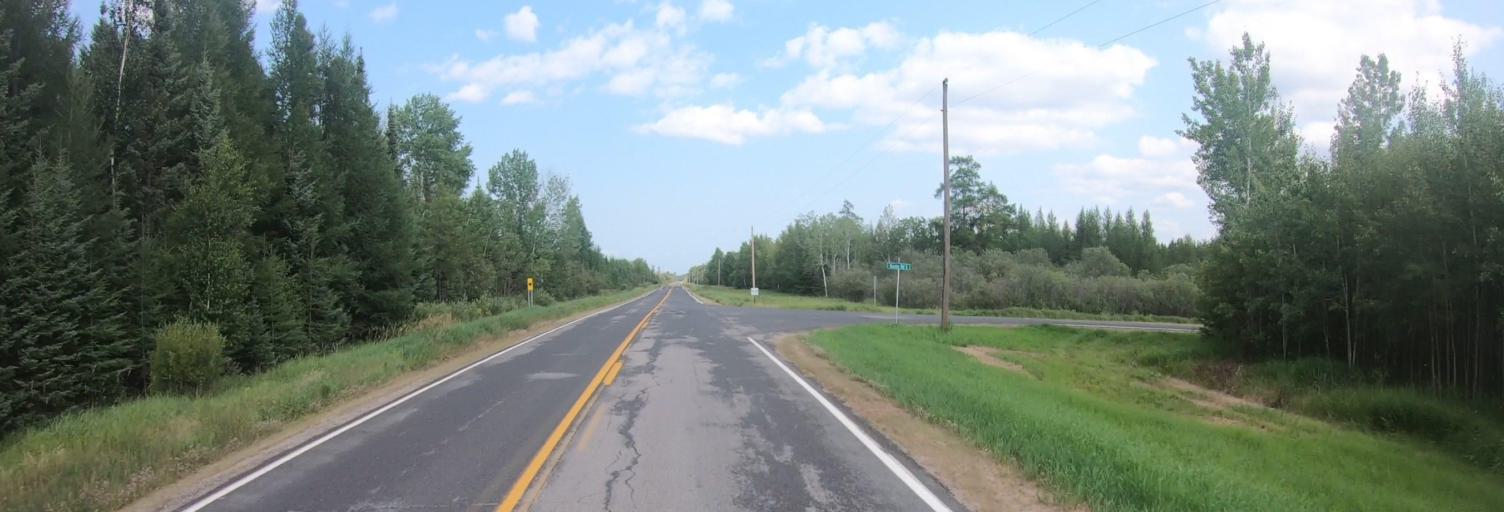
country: US
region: Minnesota
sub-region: Saint Louis County
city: Mountain Iron
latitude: 47.8917
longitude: -92.6863
